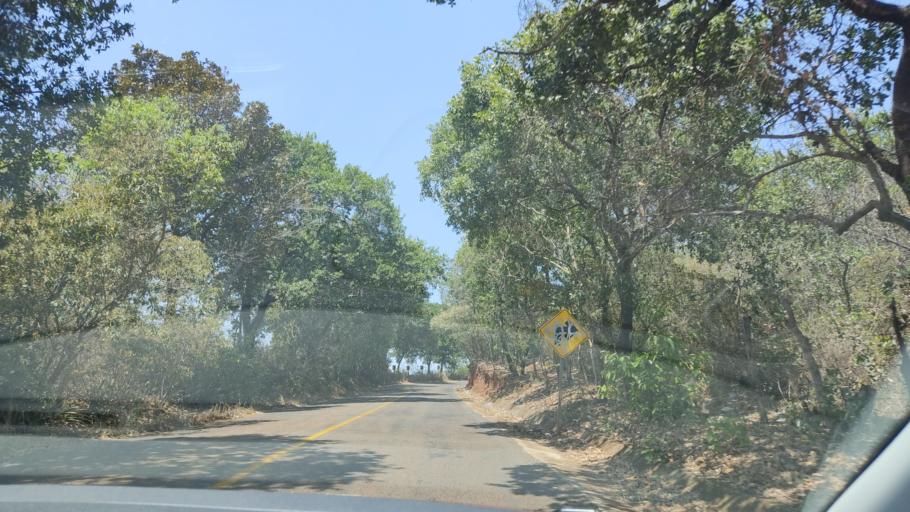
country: MX
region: Nayarit
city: Puga
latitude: 21.5810
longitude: -104.7794
